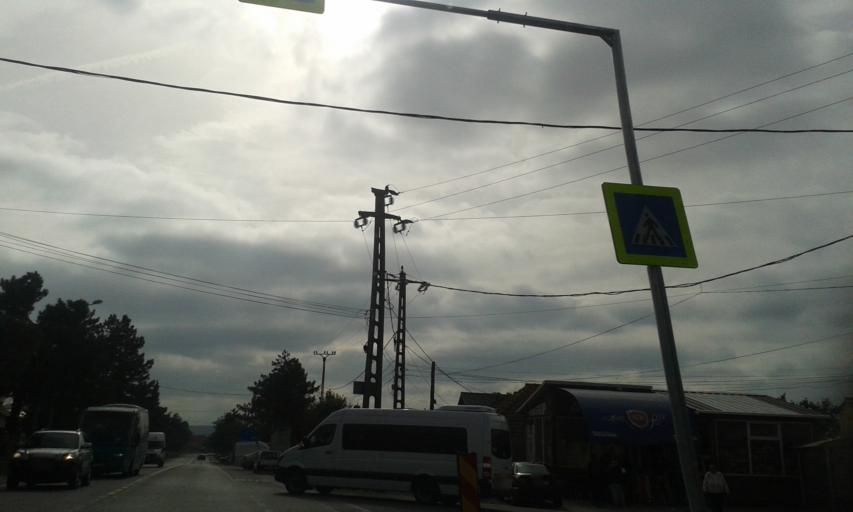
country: RO
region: Gorj
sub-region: Comuna Bumbesti-Jiu
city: Bumbesti-Jiu
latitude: 45.1773
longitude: 23.3804
